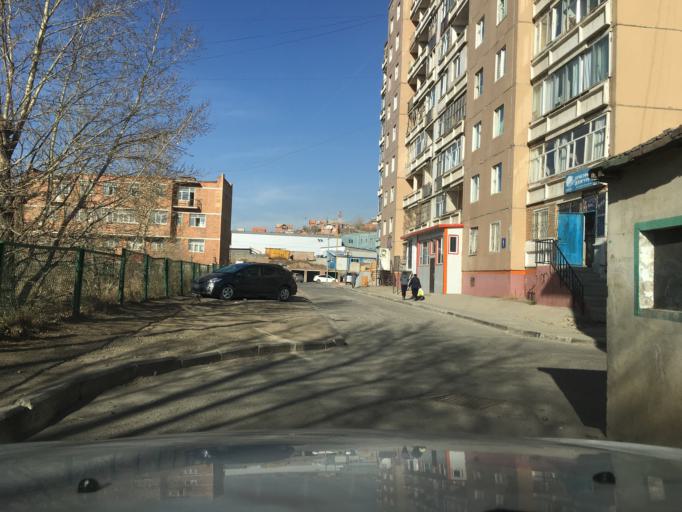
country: MN
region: Ulaanbaatar
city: Ulaanbaatar
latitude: 47.9160
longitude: 106.8509
